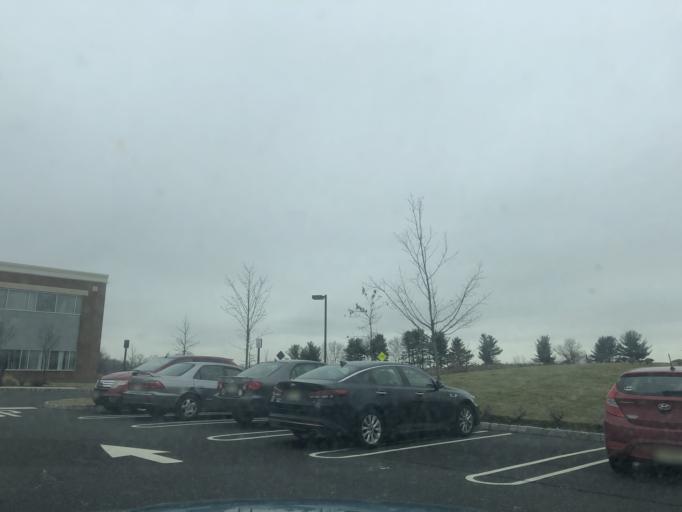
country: US
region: New Jersey
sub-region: Middlesex County
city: Plainsboro Center
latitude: 40.3435
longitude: -74.6158
